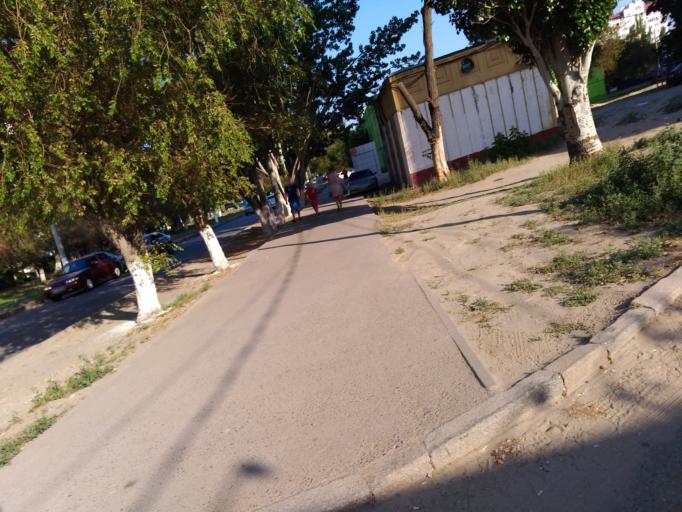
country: RU
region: Volgograd
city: Volgograd
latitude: 48.7218
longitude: 44.5118
